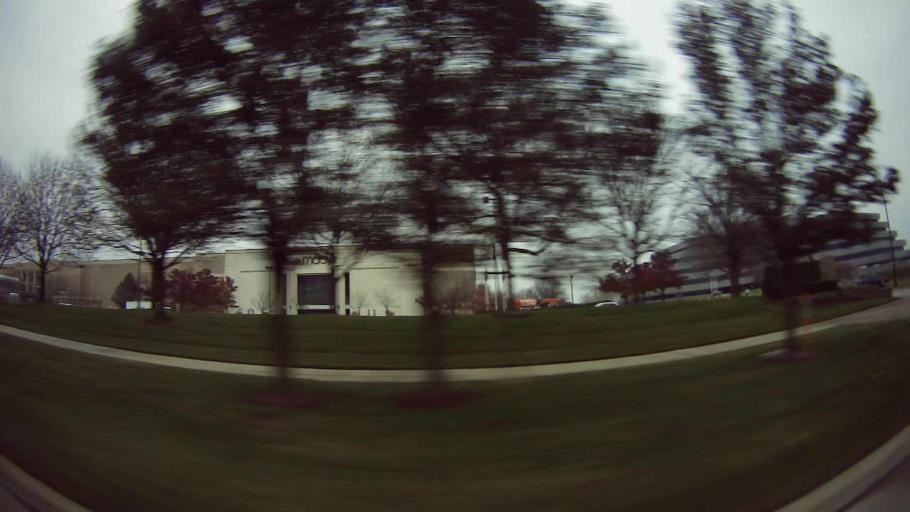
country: US
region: Michigan
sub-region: Oakland County
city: Birmingham
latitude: 42.5616
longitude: -83.1818
